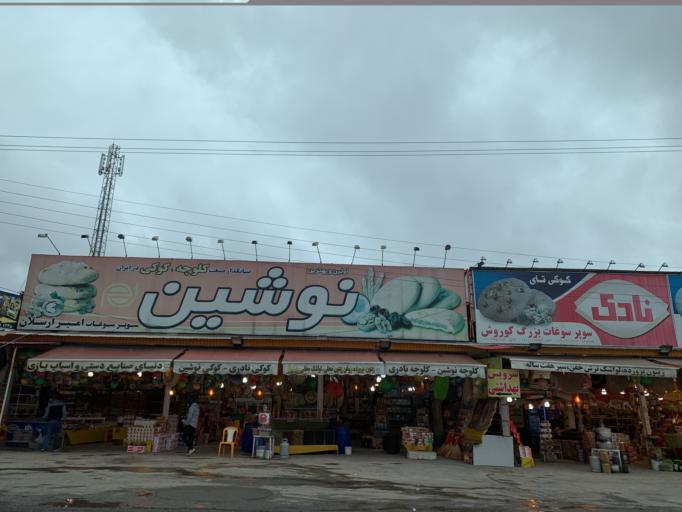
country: IR
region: Mazandaran
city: Amol
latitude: 36.4651
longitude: 52.3942
